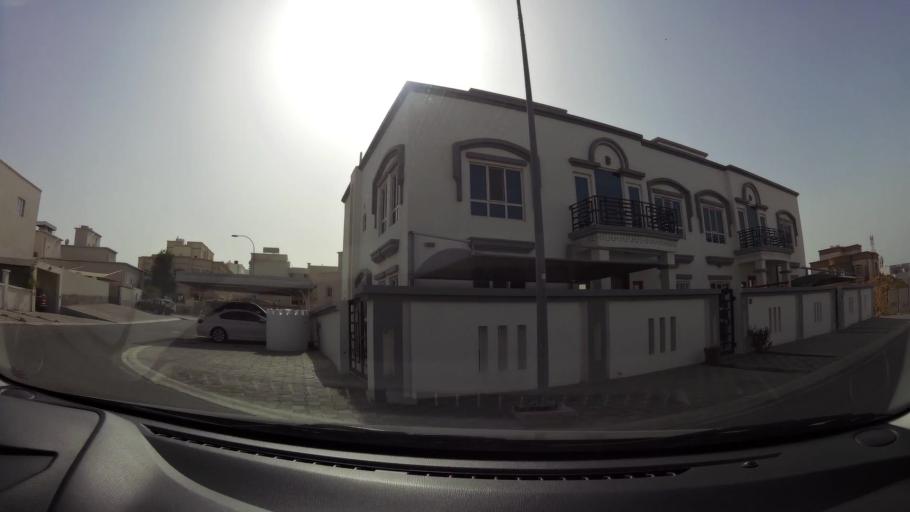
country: OM
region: Muhafazat Masqat
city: Bawshar
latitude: 23.5549
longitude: 58.3565
